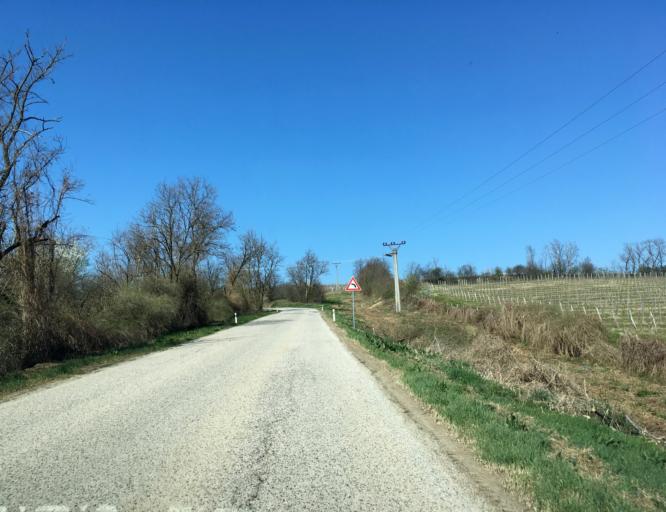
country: HU
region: Komarom-Esztergom
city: Nyergesujfalu
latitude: 47.8204
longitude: 18.6036
